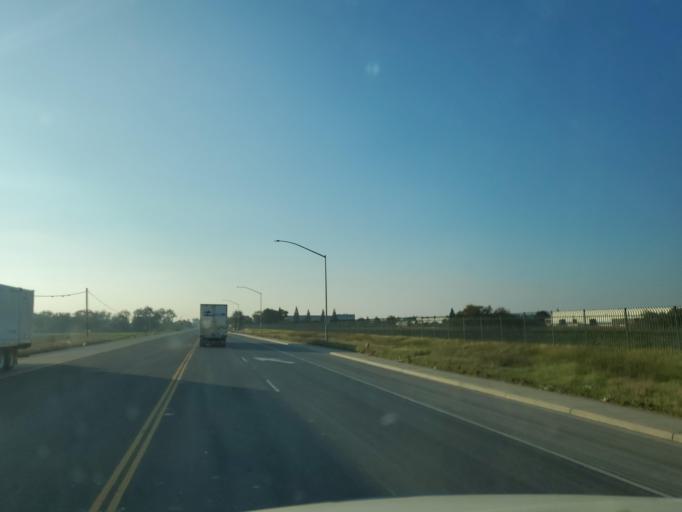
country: US
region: California
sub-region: San Joaquin County
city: Kennedy
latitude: 37.9053
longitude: -121.2039
